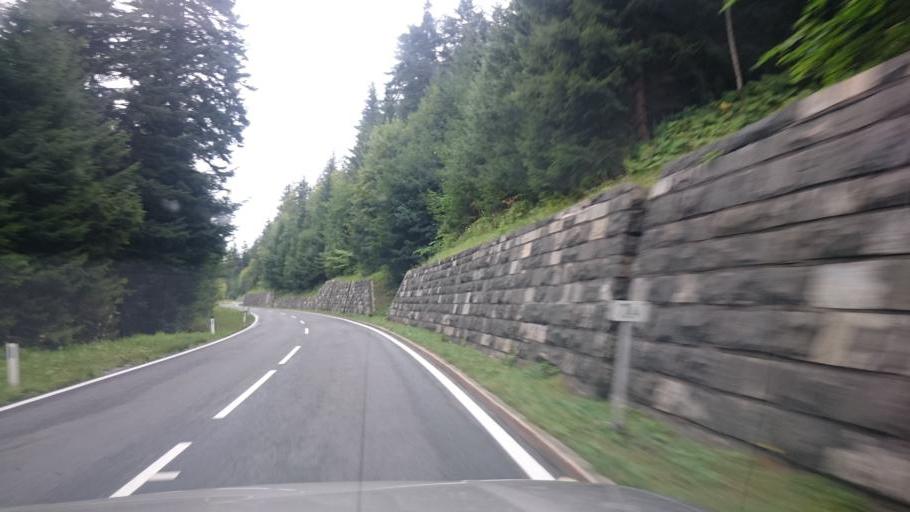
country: AT
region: Vorarlberg
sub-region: Politischer Bezirk Bregenz
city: Bildstein
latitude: 47.4266
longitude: 9.8028
